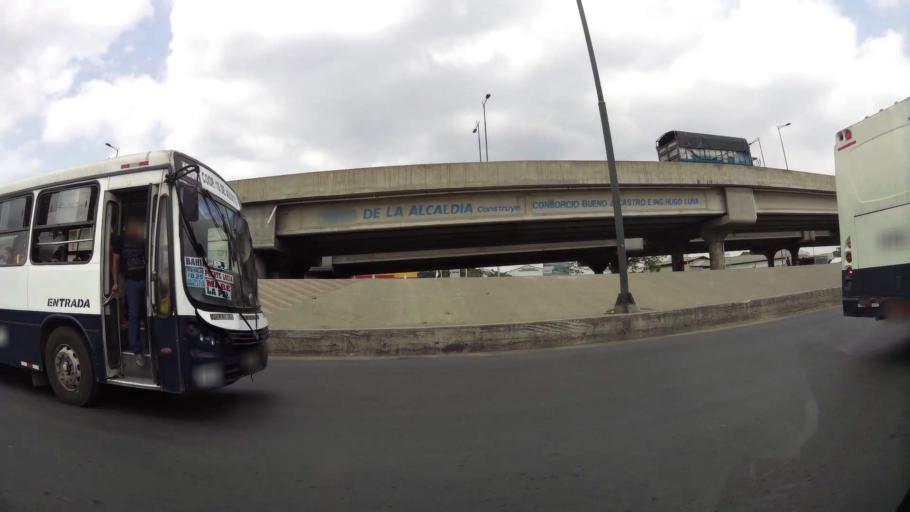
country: EC
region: Guayas
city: Santa Lucia
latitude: -2.1185
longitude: -79.9489
